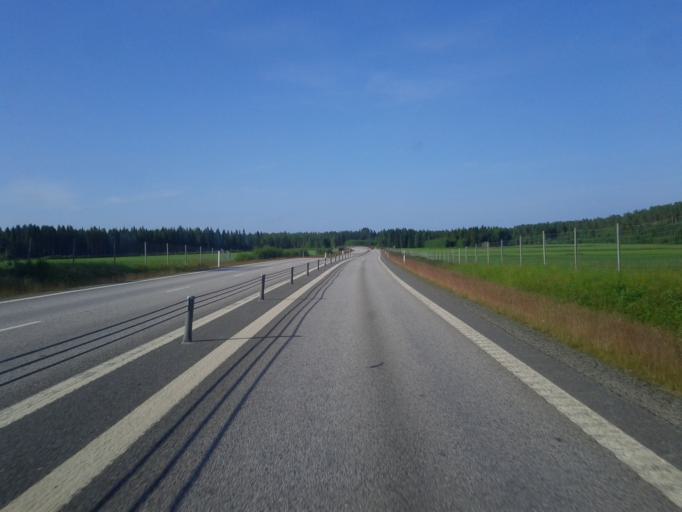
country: SE
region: Vaesterbotten
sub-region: Robertsfors Kommun
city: Robertsfors
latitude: 64.1059
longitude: 20.8745
